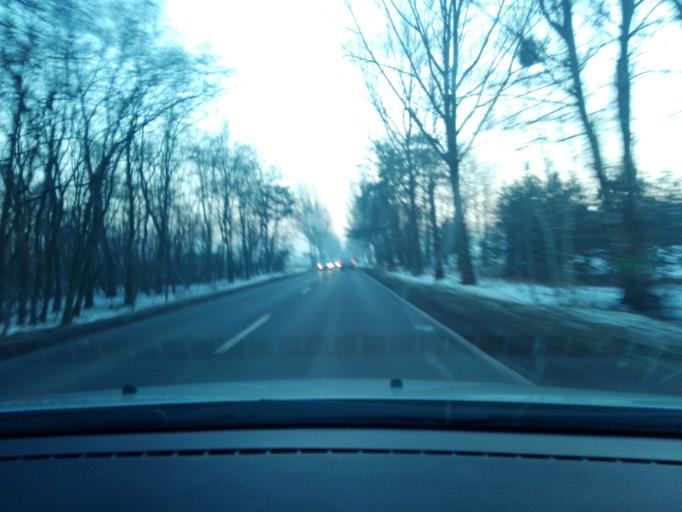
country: PL
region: Lodz Voivodeship
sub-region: Powiat zgierski
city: Zgierz
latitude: 51.9046
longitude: 19.4286
